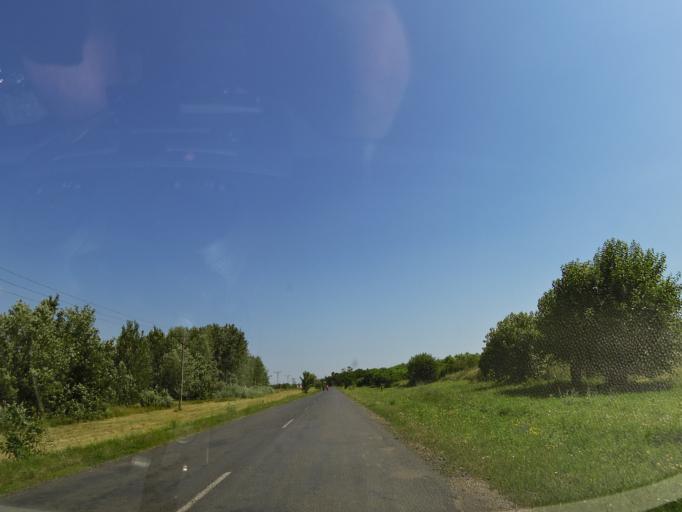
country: HU
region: Jasz-Nagykun-Szolnok
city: Abadszalok
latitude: 47.4650
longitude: 20.5908
